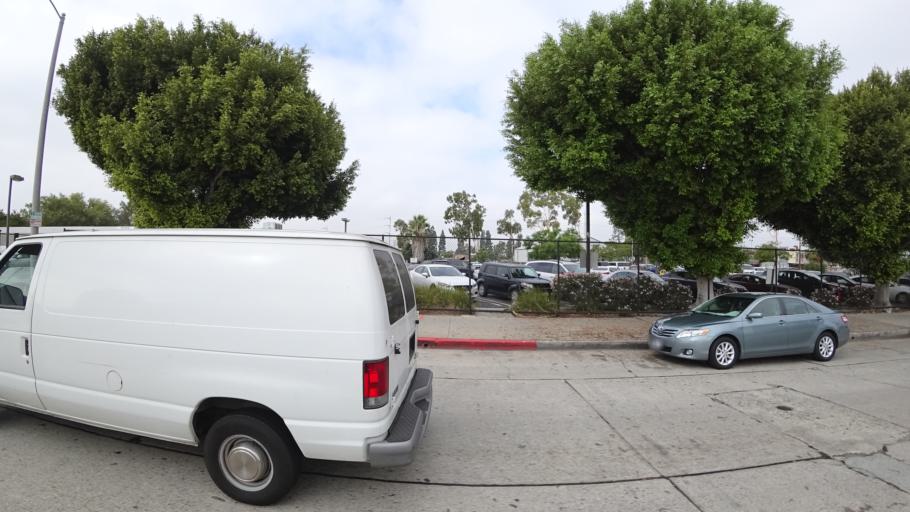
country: US
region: California
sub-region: Los Angeles County
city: Inglewood
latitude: 33.9707
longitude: -118.3571
